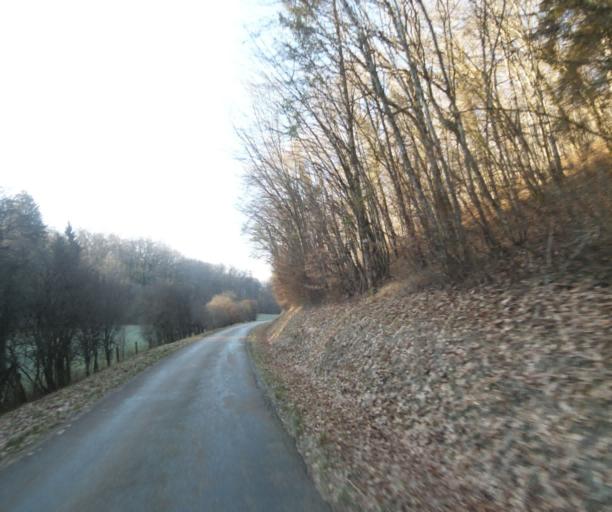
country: FR
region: Champagne-Ardenne
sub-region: Departement de la Haute-Marne
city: Joinville
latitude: 48.4895
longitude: 5.2284
